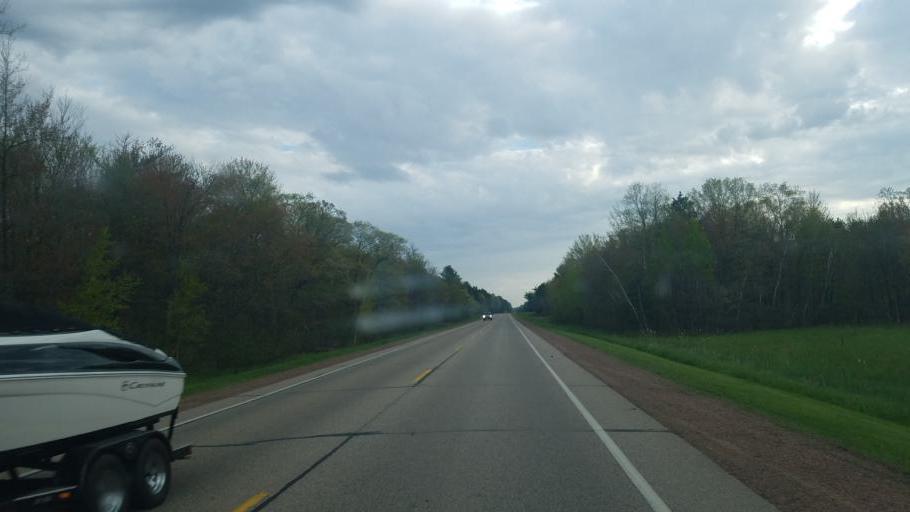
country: US
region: Wisconsin
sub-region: Wood County
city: Nekoosa
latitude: 44.3117
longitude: -90.1109
